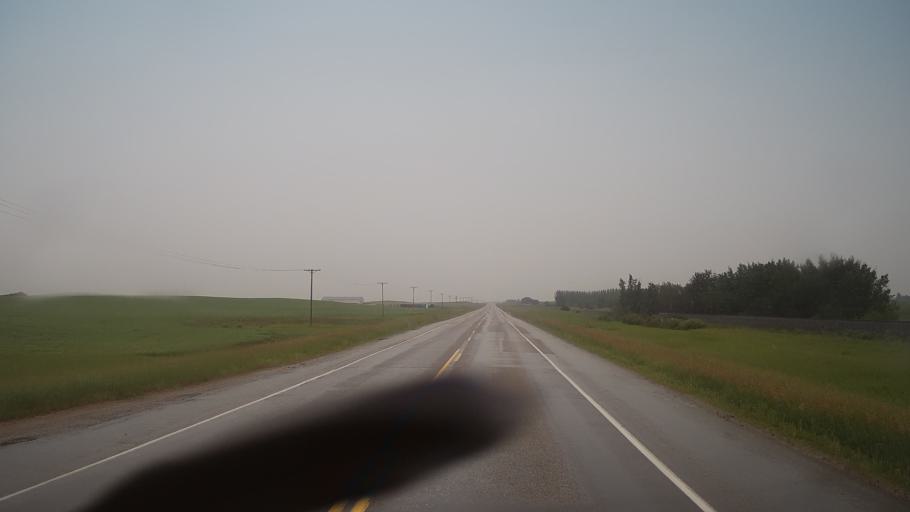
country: CA
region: Saskatchewan
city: Biggar
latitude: 52.0856
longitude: -108.0415
